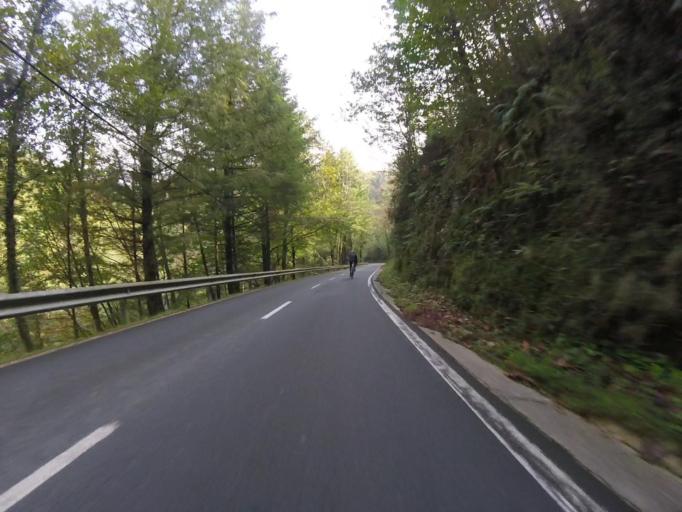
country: ES
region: Navarre
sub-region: Provincia de Navarra
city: Goizueta
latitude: 43.1950
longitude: -1.8577
